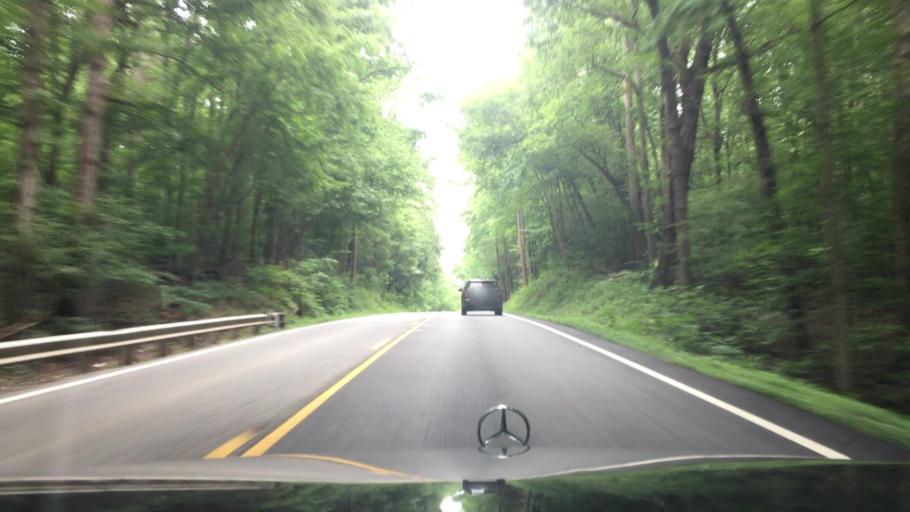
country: US
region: Virginia
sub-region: Nottoway County
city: Crewe
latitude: 37.2734
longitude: -78.1488
